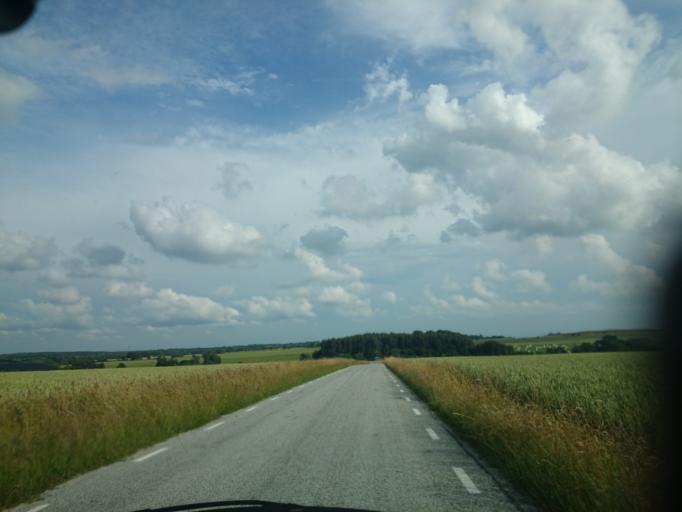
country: SE
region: Skane
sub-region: Lunds Kommun
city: Lund
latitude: 55.7178
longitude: 13.3010
